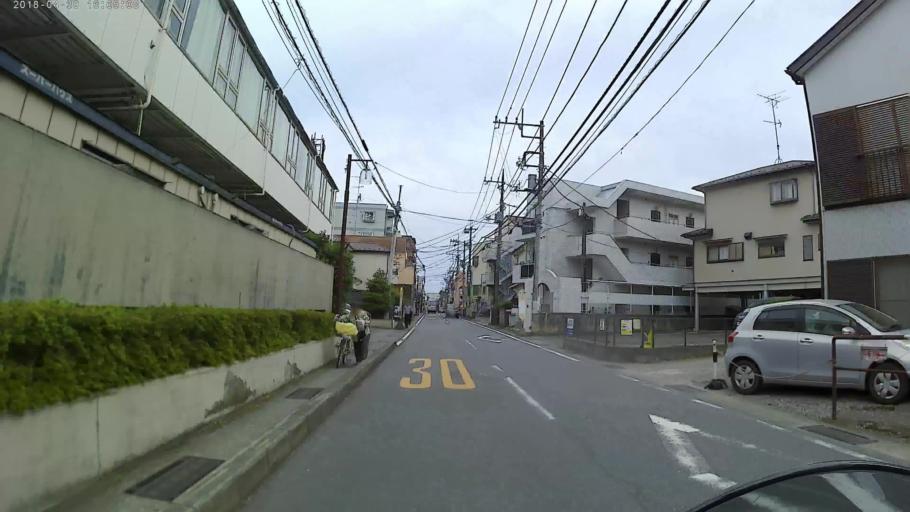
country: JP
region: Kanagawa
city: Minami-rinkan
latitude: 35.5064
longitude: 139.4258
